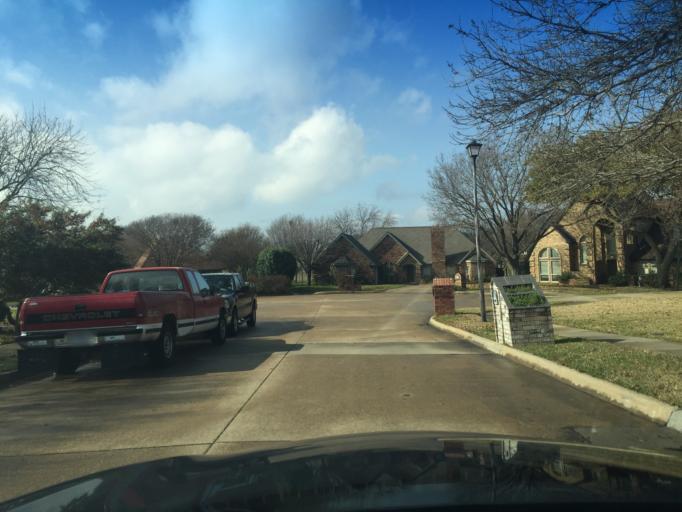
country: US
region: Texas
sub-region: Dallas County
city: Carrollton
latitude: 32.9962
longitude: -96.8797
